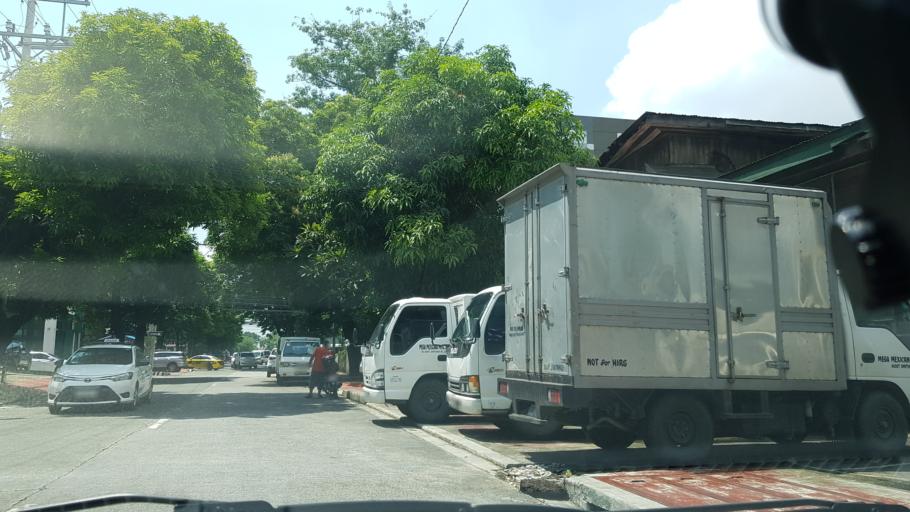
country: PH
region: Calabarzon
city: Del Monte
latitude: 14.6310
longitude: 121.0279
